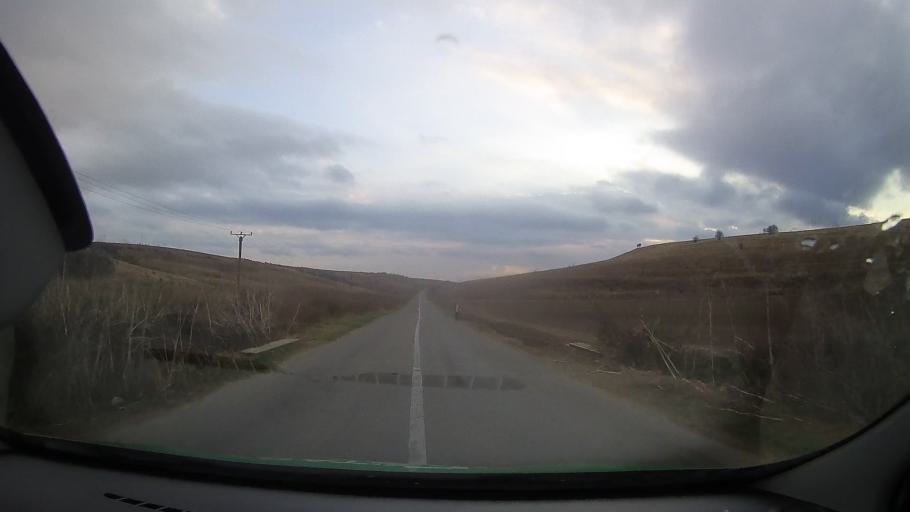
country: RO
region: Constanta
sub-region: Comuna Dobromir
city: Dobromir
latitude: 44.0350
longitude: 27.8023
